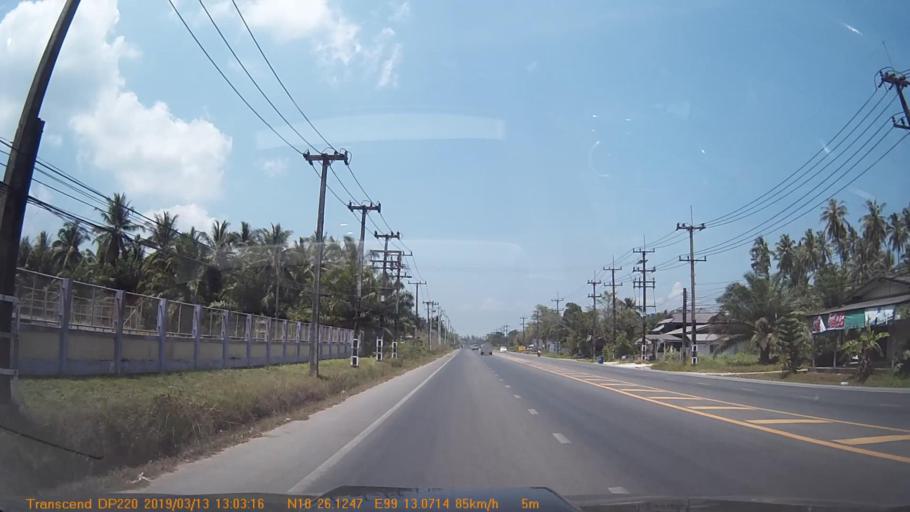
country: TH
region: Chumphon
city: Chumphon
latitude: 10.4360
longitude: 99.2176
